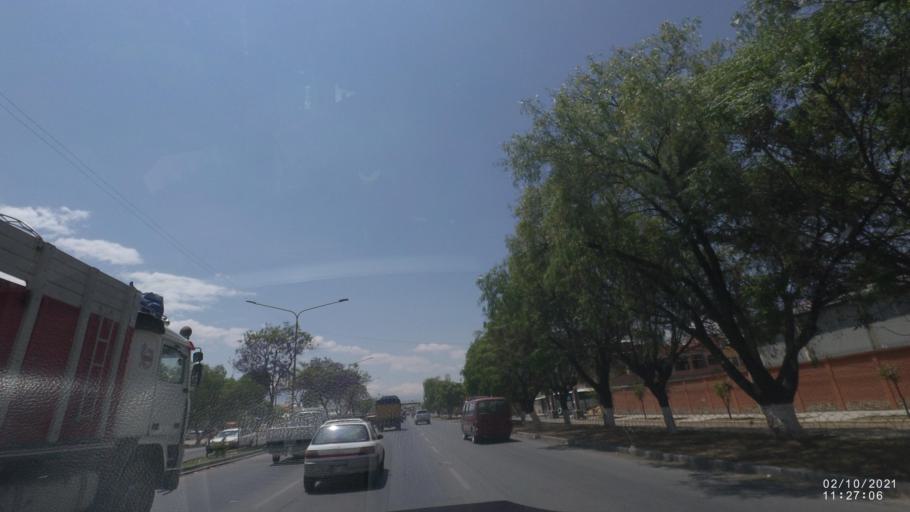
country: BO
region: Cochabamba
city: Cochabamba
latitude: -17.3917
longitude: -66.2554
